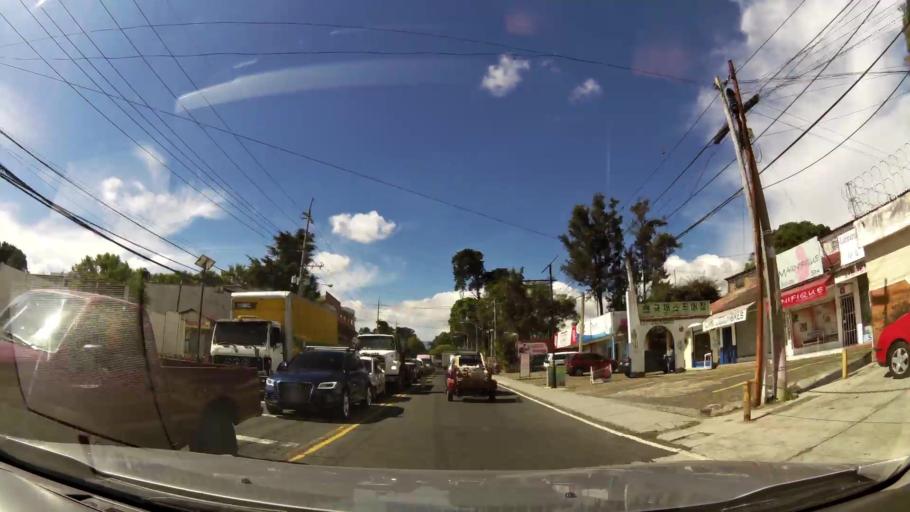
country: GT
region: Guatemala
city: Guatemala City
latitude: 14.6309
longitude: -90.5593
